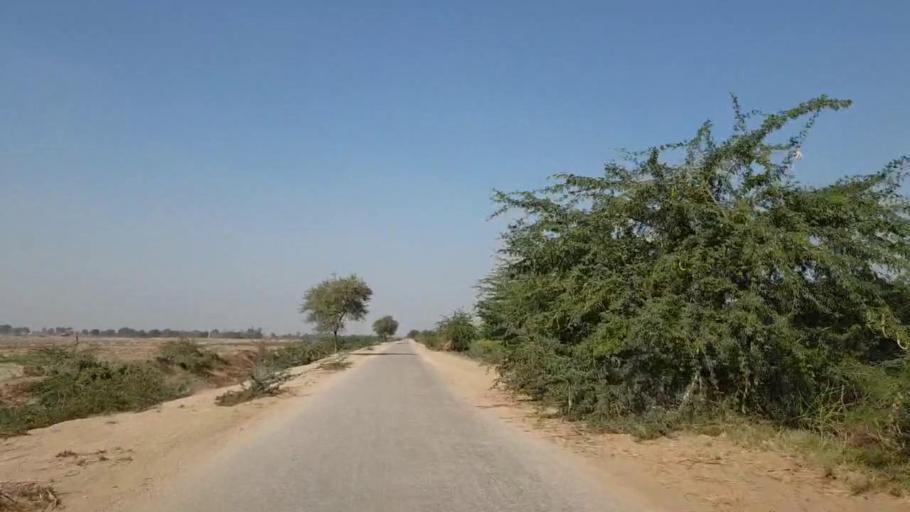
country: PK
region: Sindh
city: Digri
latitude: 25.0163
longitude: 69.1060
